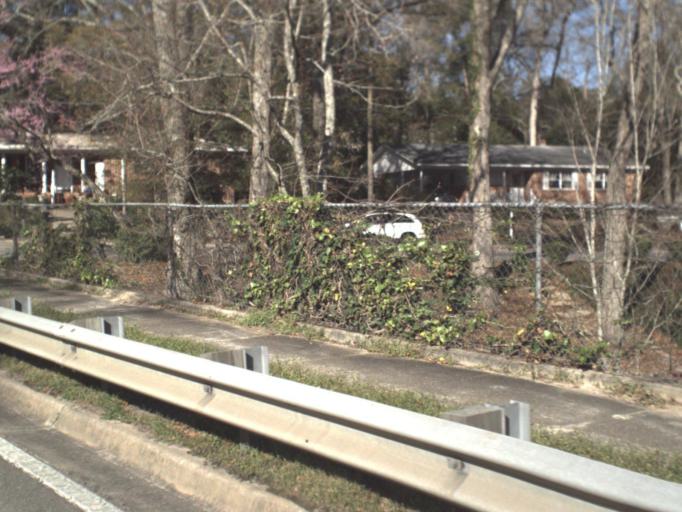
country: US
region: Florida
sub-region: Leon County
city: Tallahassee
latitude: 30.4513
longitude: -84.2627
